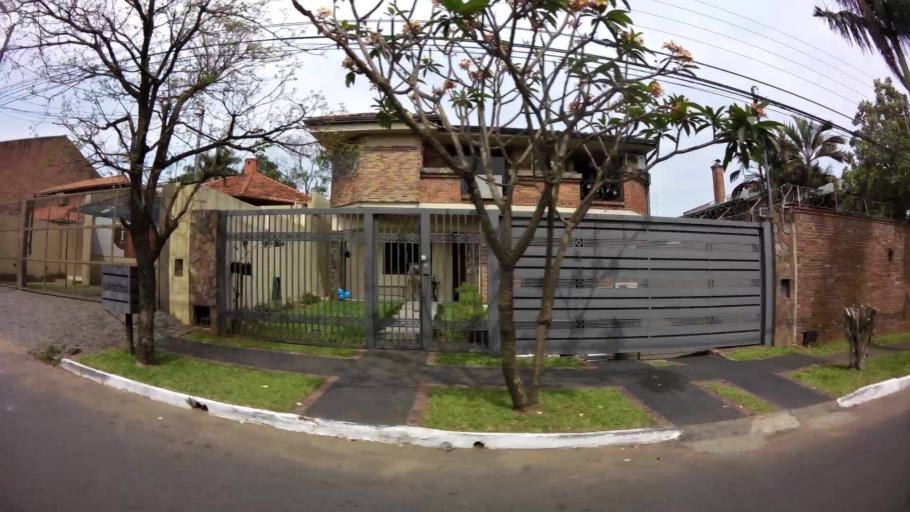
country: PY
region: Asuncion
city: Asuncion
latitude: -25.2756
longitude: -57.5650
